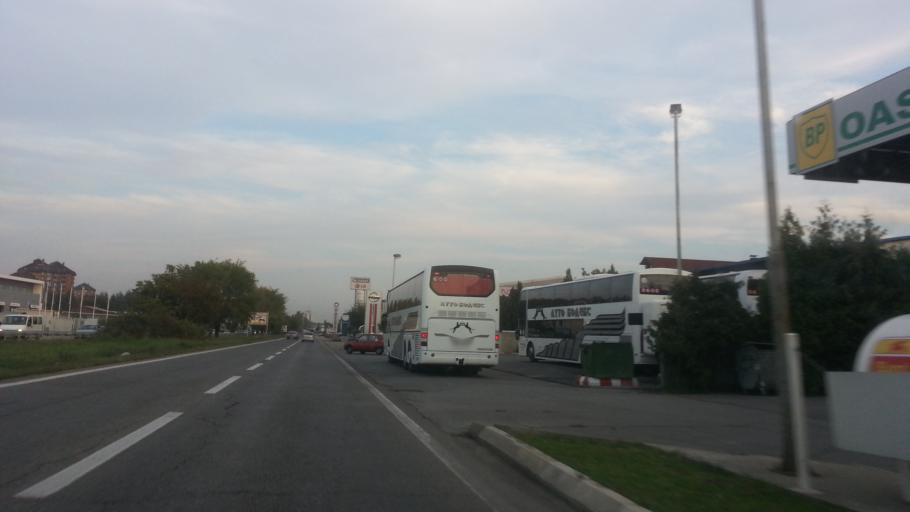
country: RS
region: Central Serbia
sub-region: Belgrade
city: Zemun
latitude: 44.8578
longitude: 20.3595
